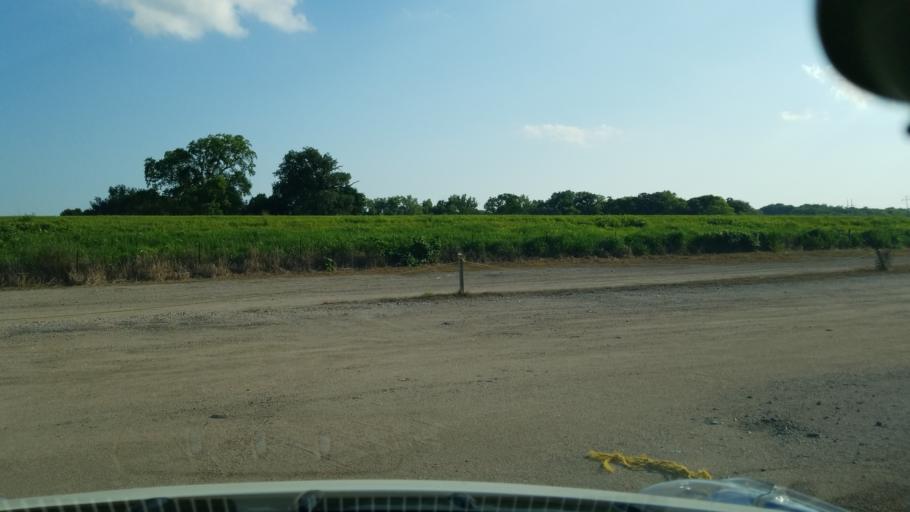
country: US
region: Nebraska
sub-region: Sarpy County
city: Papillion
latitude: 41.1517
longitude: -95.9942
